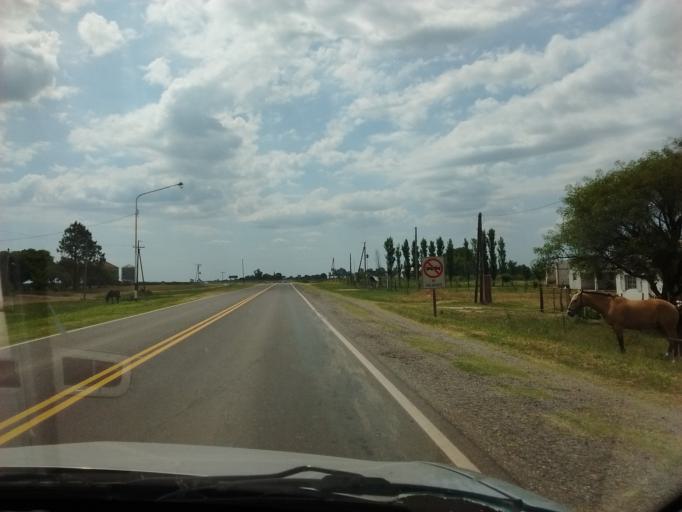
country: AR
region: Entre Rios
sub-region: Departamento de Victoria
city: Victoria
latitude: -32.7750
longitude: -59.9163
